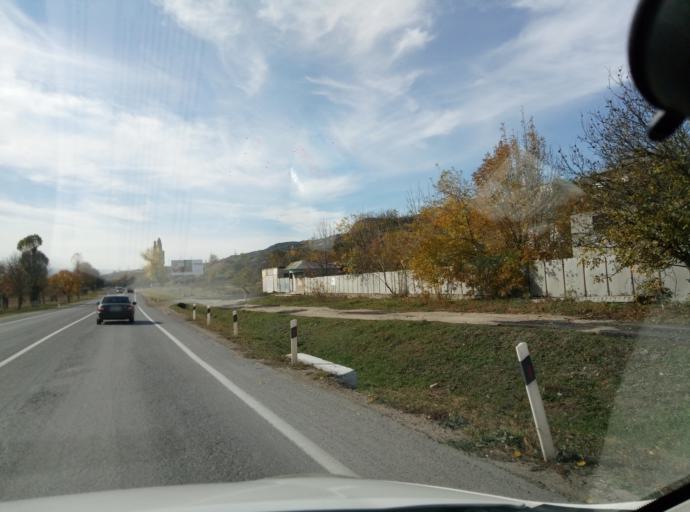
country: RU
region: Stavropol'skiy
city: Yasnaya Polyana
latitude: 43.9607
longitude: 42.7683
